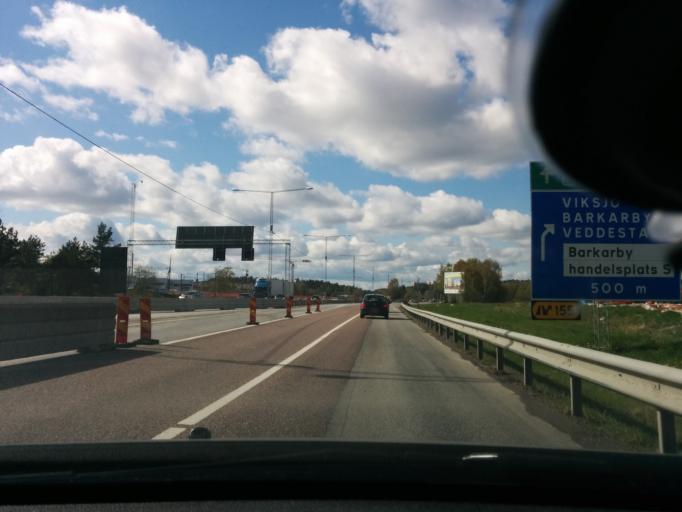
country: SE
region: Stockholm
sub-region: Jarfalla Kommun
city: Jakobsberg
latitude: 59.4051
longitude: 17.8667
